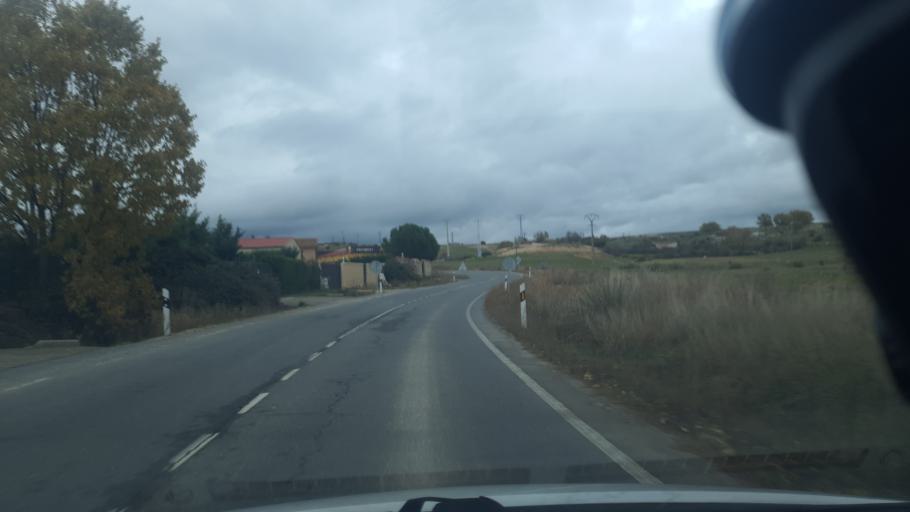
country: ES
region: Castille and Leon
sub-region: Provincia de Segovia
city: La Lastrilla
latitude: 40.9753
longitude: -4.0865
